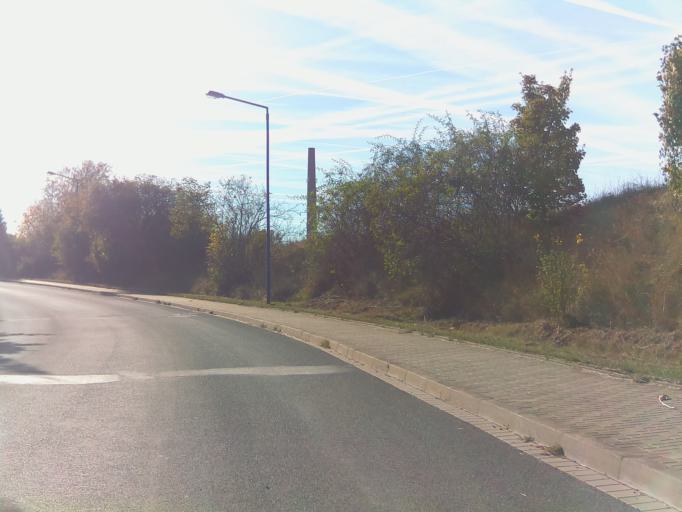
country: DE
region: Thuringia
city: Stadtilm
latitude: 50.7786
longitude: 11.0963
